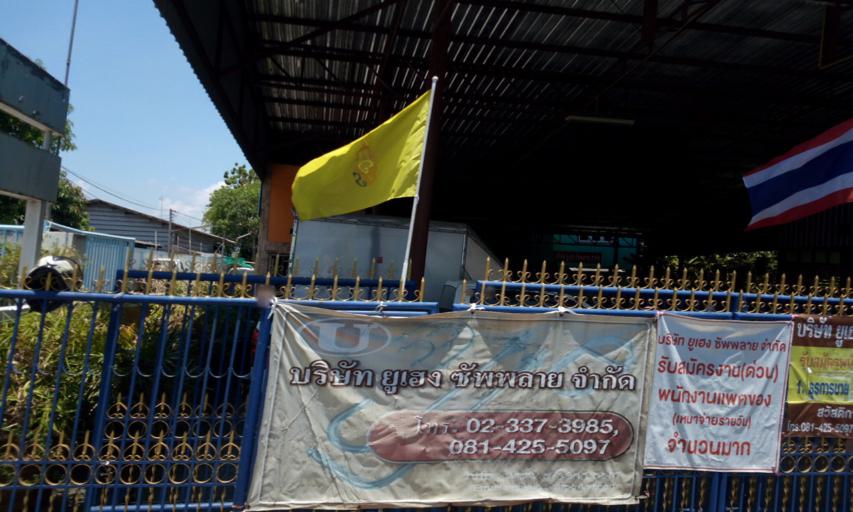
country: TH
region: Bangkok
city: Bang Na
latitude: 13.6084
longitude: 100.7080
